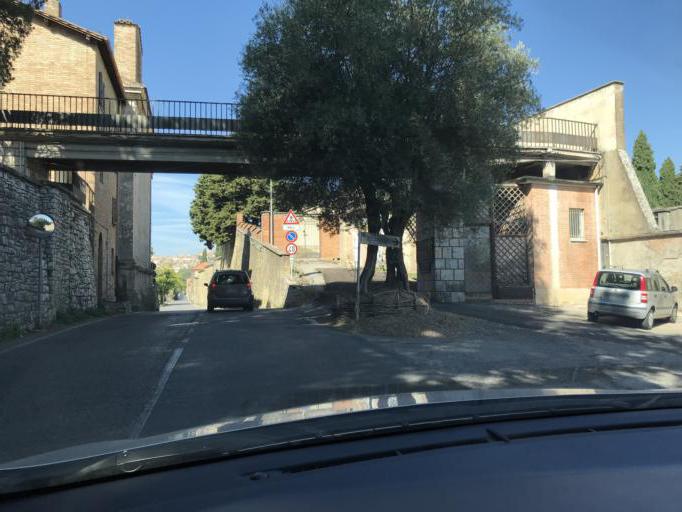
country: IT
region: Umbria
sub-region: Provincia di Perugia
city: Perugia
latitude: 43.1102
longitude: 12.4172
